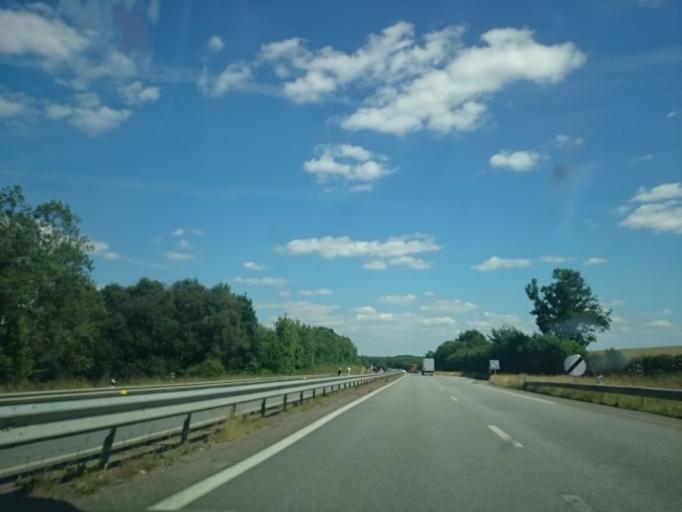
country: FR
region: Brittany
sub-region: Departement des Cotes-d'Armor
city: Loudeac
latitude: 48.1858
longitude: -2.7421
